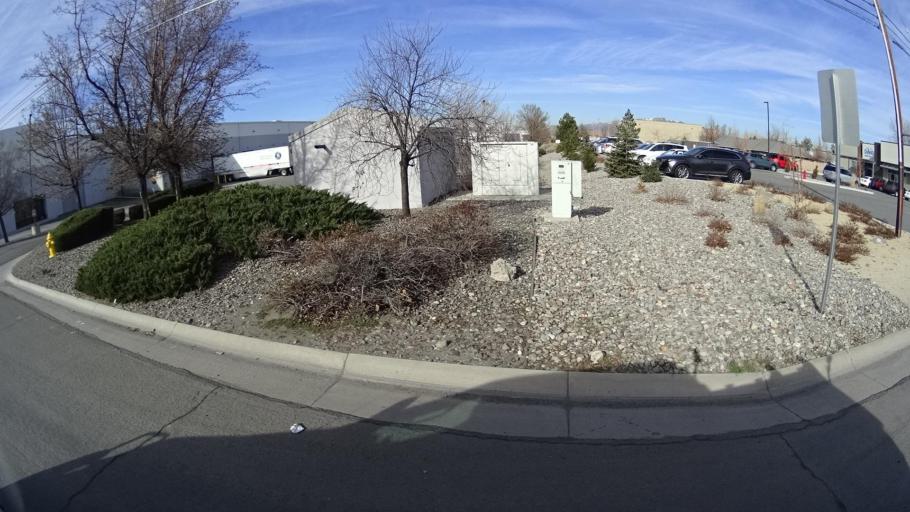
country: US
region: Nevada
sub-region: Washoe County
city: Sparks
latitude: 39.5411
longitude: -119.7035
